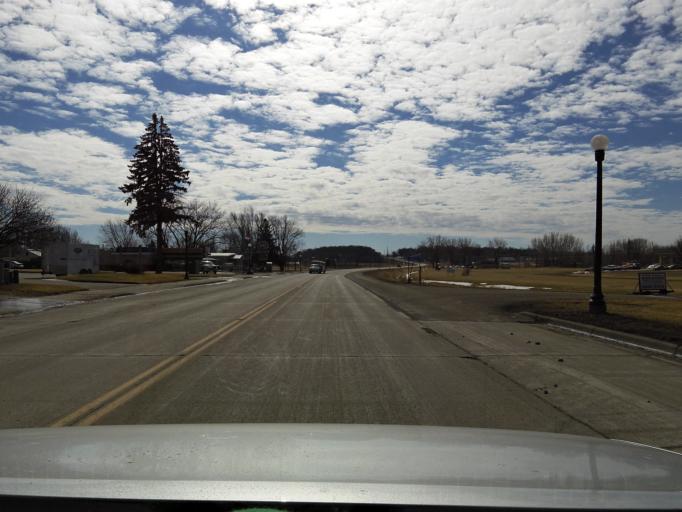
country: US
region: Minnesota
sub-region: Le Sueur County
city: New Prague
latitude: 44.5407
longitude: -93.5842
